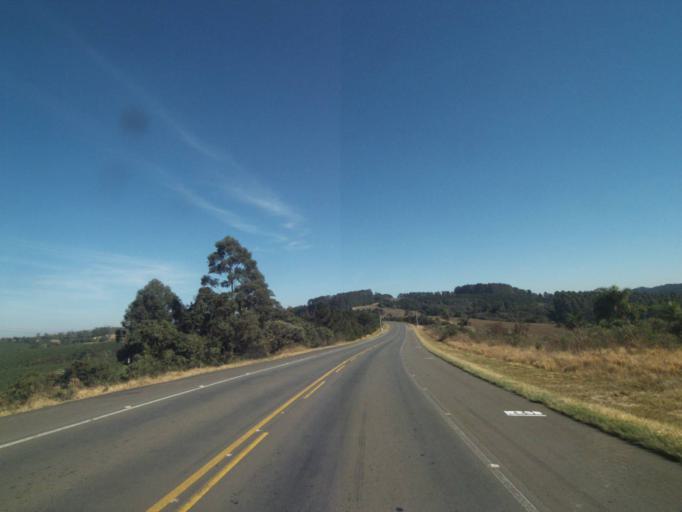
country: BR
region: Parana
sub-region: Tibagi
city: Tibagi
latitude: -24.8080
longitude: -50.4755
